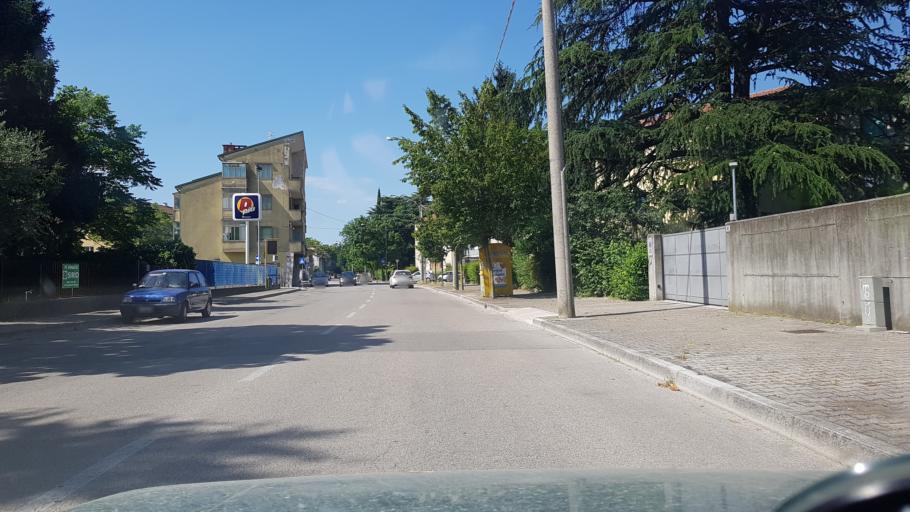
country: SI
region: Nova Gorica
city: Nova Gorica
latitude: 45.9578
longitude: 13.6328
